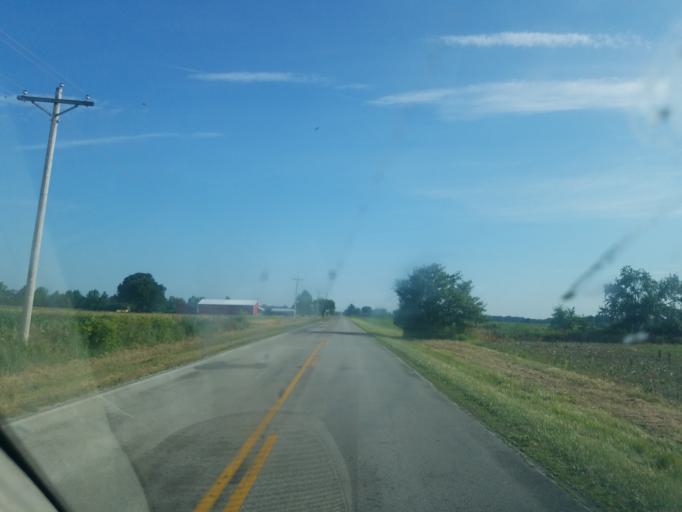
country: US
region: Ohio
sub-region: Hardin County
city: Forest
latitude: 40.7625
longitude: -83.4196
